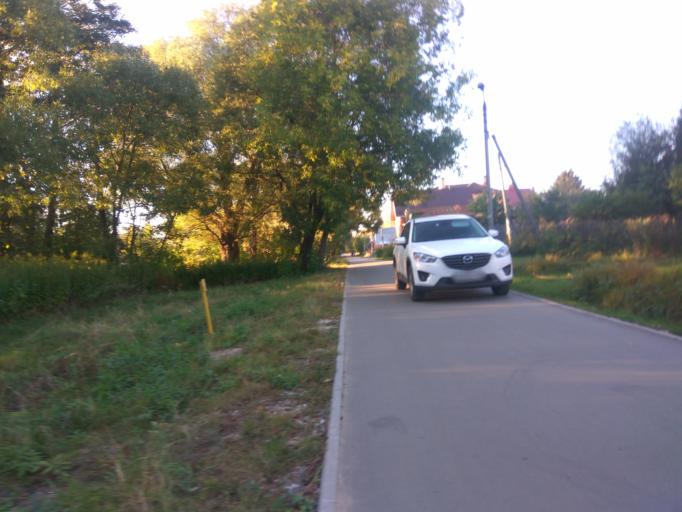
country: RU
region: Moskovskaya
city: Yegor'yevsk
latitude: 55.3736
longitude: 39.0390
